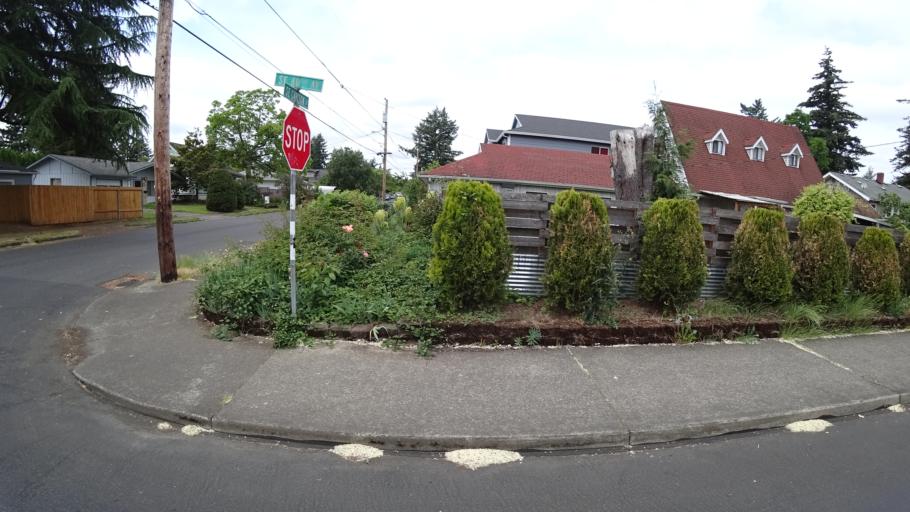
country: US
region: Oregon
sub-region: Multnomah County
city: Lents
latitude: 45.4784
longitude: -122.5817
